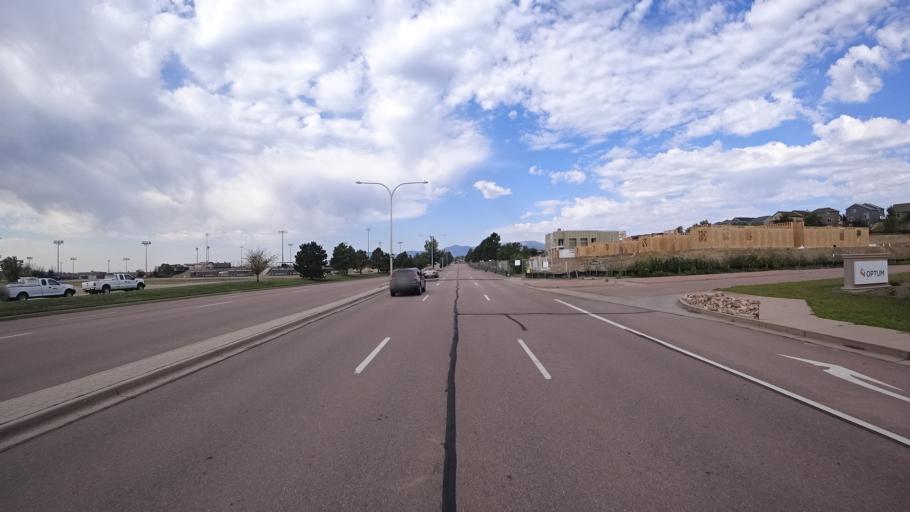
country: US
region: Colorado
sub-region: El Paso County
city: Cimarron Hills
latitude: 38.8975
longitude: -104.7099
